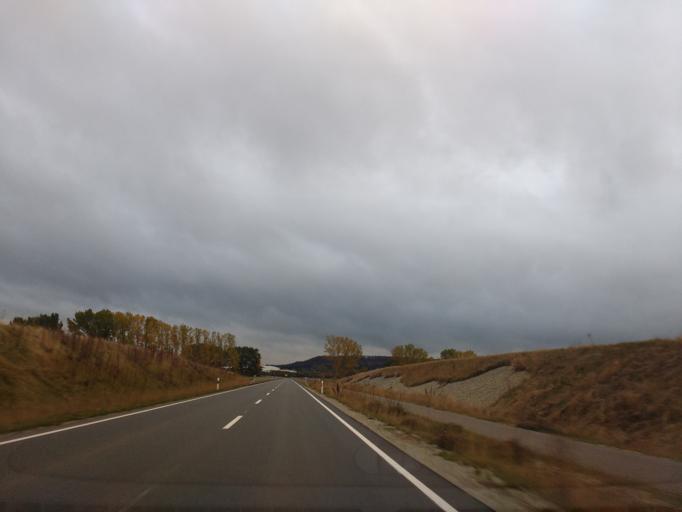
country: DE
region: Thuringia
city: Grossbodungen
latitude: 51.4612
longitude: 10.4614
